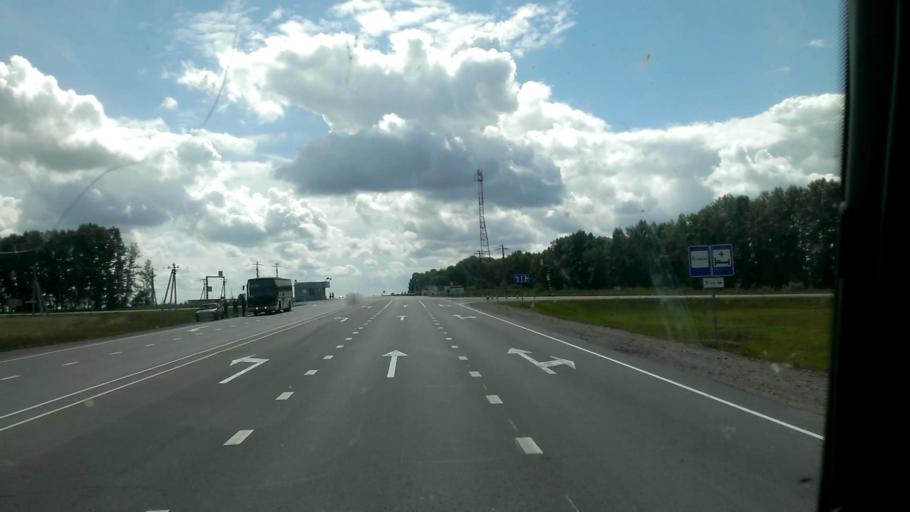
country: RU
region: Altai Krai
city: Troitskoye
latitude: 52.9680
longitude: 84.7502
